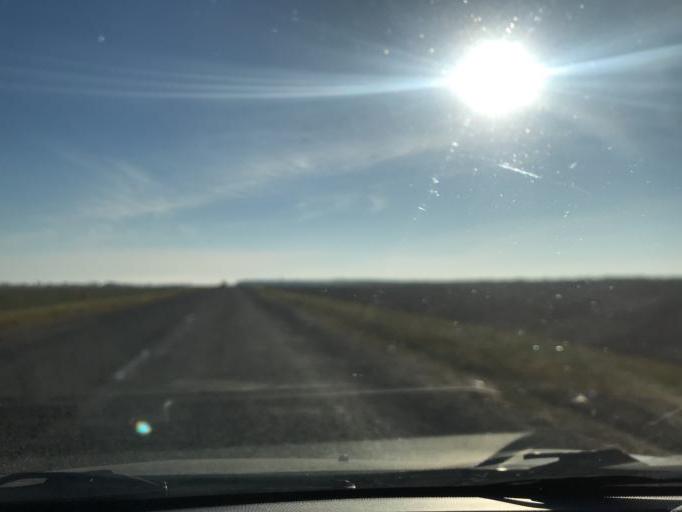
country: BY
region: Gomel
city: Brahin
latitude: 51.7901
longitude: 30.1804
